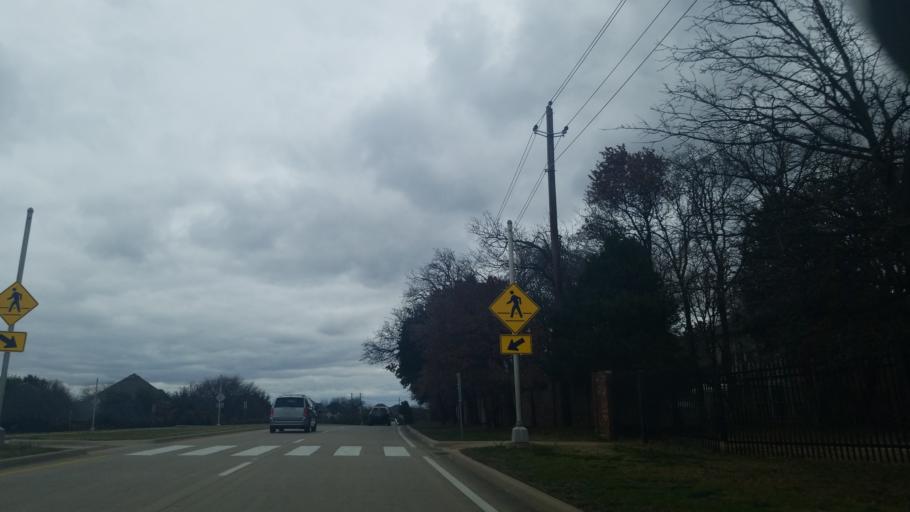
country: US
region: Texas
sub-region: Denton County
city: Copper Canyon
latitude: 33.0963
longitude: -97.0804
